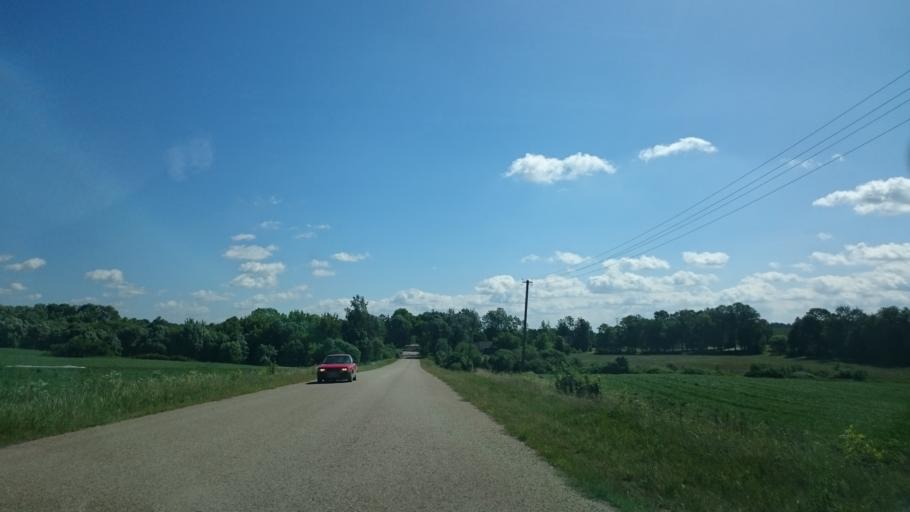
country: LV
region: Cibla
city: Cibla
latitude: 56.5350
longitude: 27.8579
